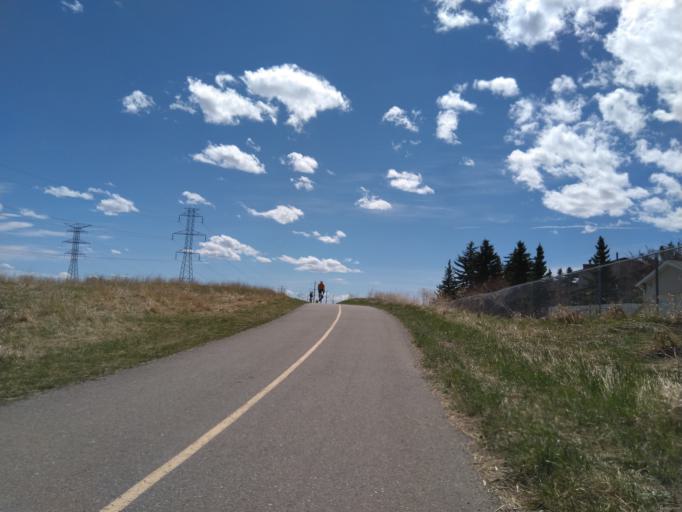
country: CA
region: Alberta
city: Calgary
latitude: 51.0460
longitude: -114.1654
